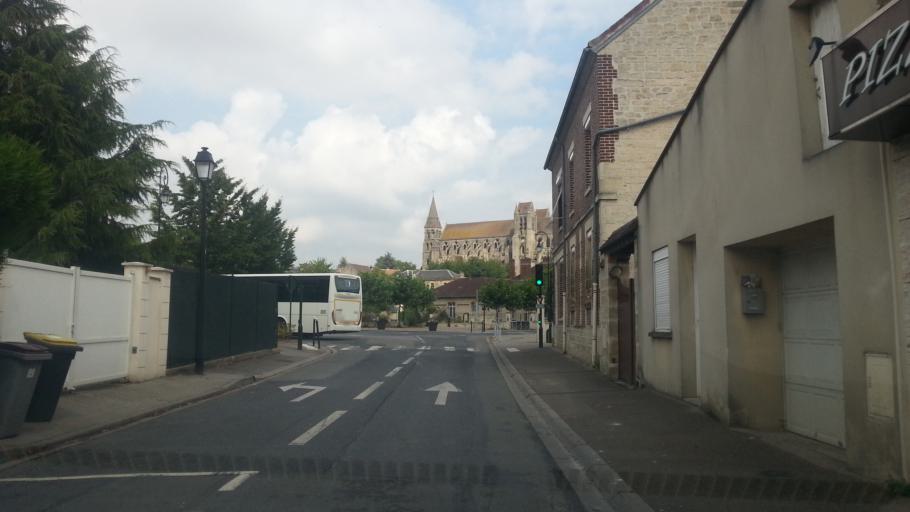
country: FR
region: Picardie
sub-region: Departement de l'Oise
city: Villers-sous-Saint-Leu
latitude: 49.2157
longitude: 2.4193
